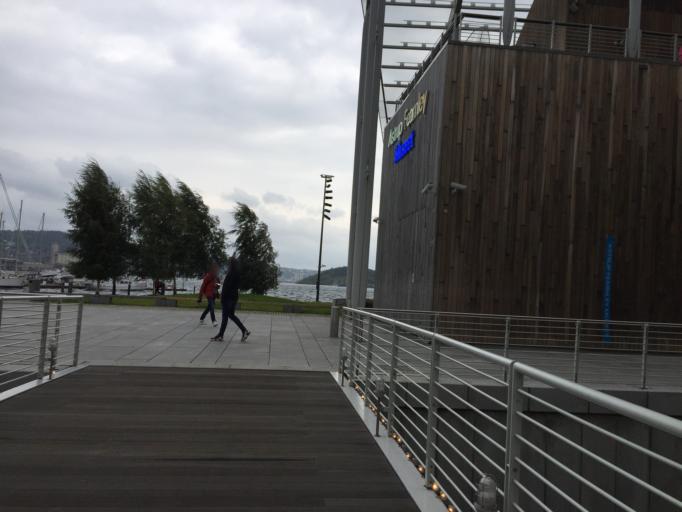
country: NO
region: Oslo
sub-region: Oslo
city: Oslo
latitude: 59.9075
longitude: 10.7221
